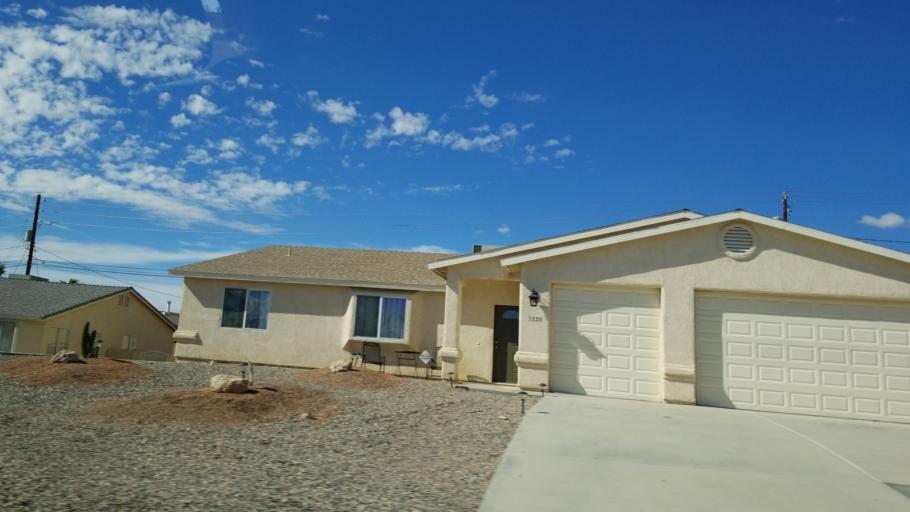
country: US
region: Arizona
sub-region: Mohave County
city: Lake Havasu City
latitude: 34.4928
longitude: -114.2942
